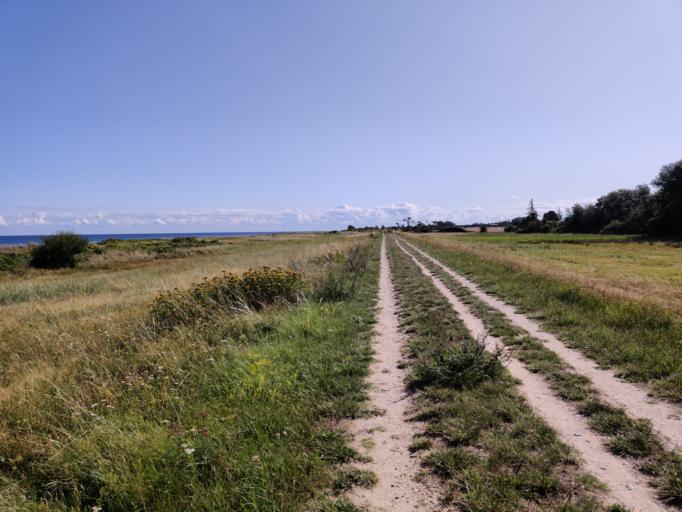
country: DK
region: Zealand
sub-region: Guldborgsund Kommune
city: Nykobing Falster
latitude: 54.5825
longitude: 11.9718
